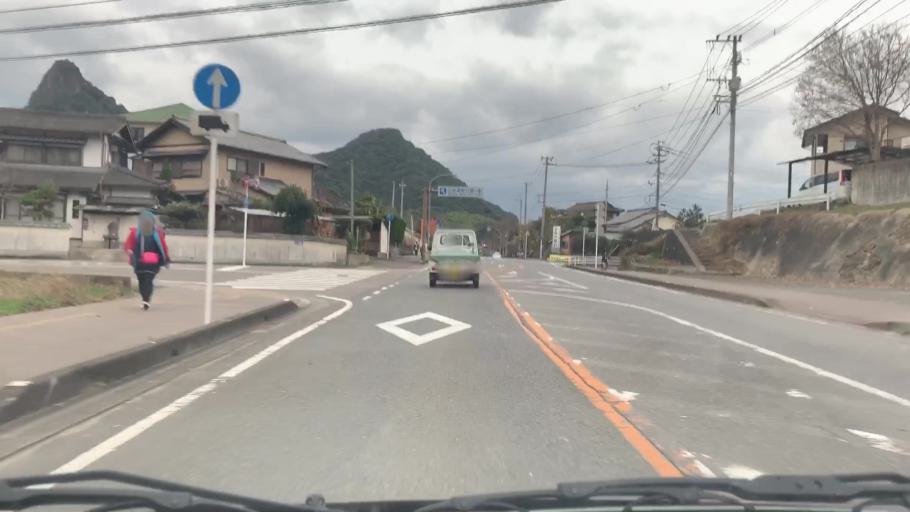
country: JP
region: Saga Prefecture
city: Takeocho-takeo
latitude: 33.1872
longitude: 130.0286
